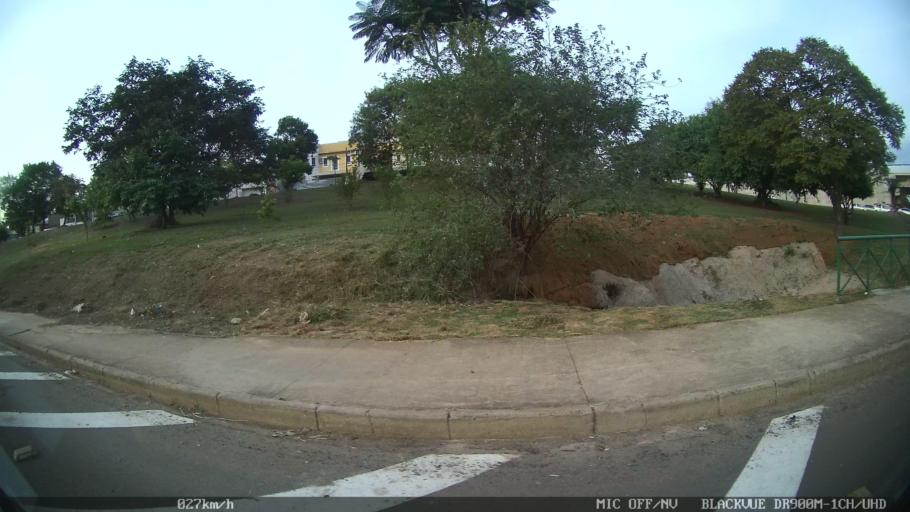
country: BR
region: Sao Paulo
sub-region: Limeira
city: Limeira
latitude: -22.5829
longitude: -47.4101
